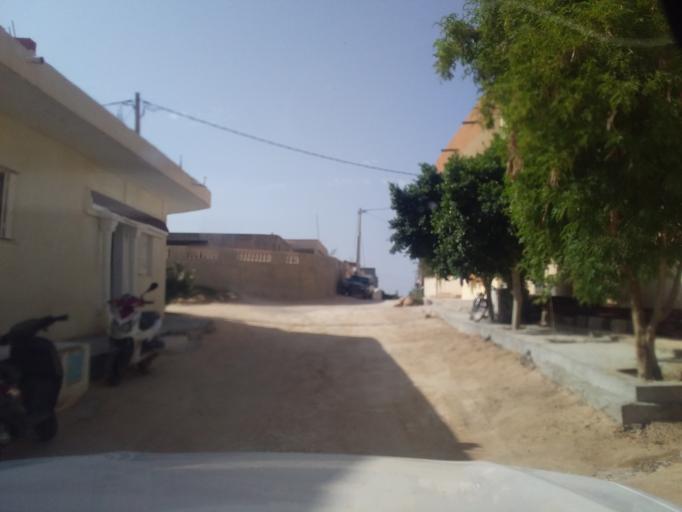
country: TN
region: Qabis
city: Gabes
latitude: 33.6348
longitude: 10.2853
